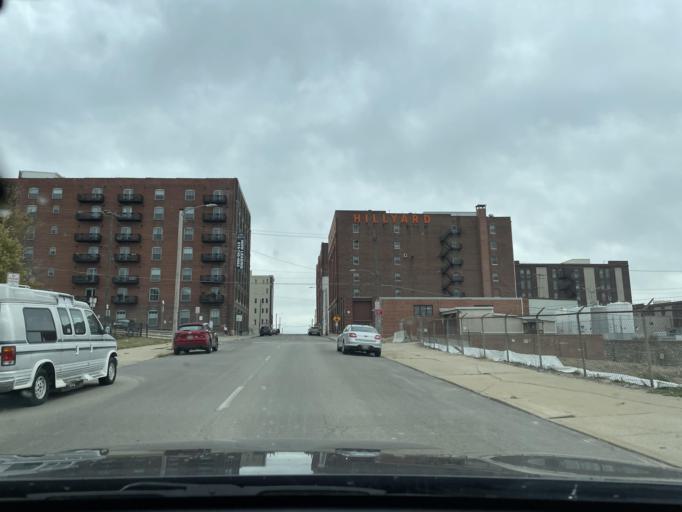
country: US
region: Missouri
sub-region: Buchanan County
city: Saint Joseph
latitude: 39.7702
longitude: -94.8567
